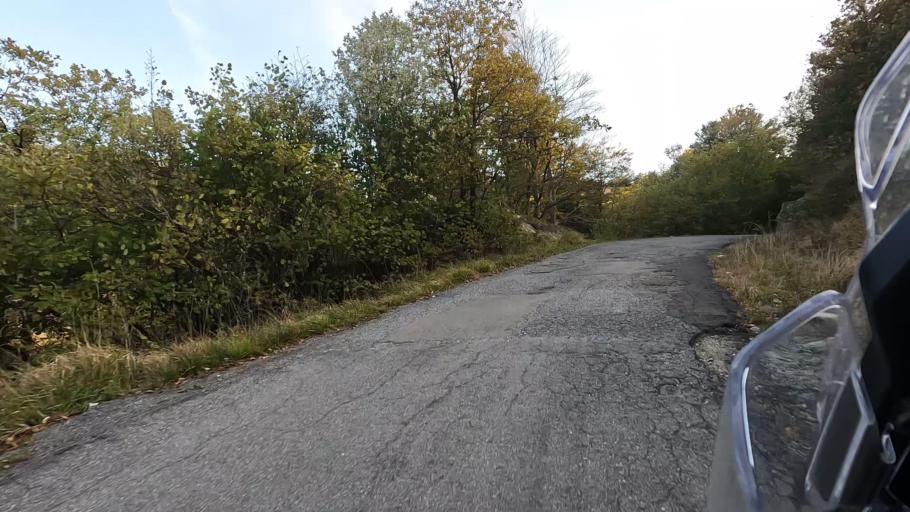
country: IT
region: Liguria
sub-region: Provincia di Genova
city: Sciarborasca
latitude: 44.4367
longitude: 8.5852
